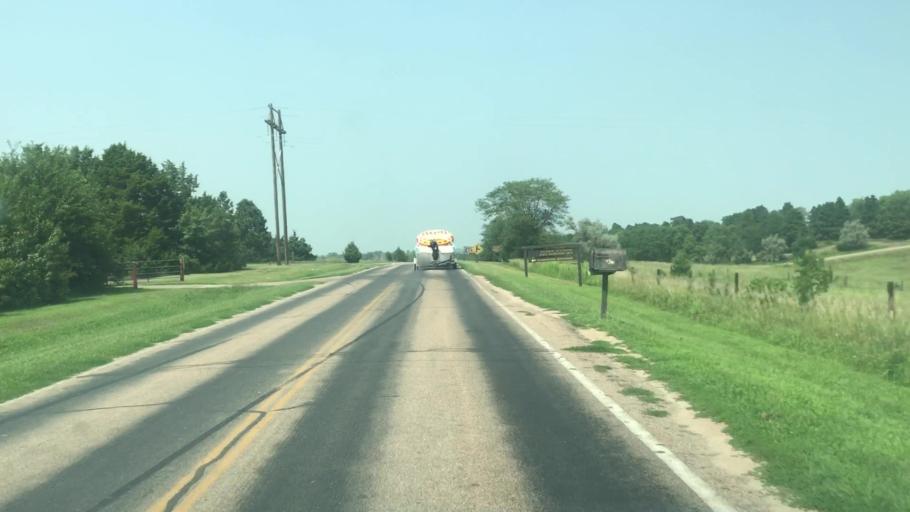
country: US
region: Nebraska
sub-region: Sherman County
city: Loup City
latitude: 41.2858
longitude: -98.8998
